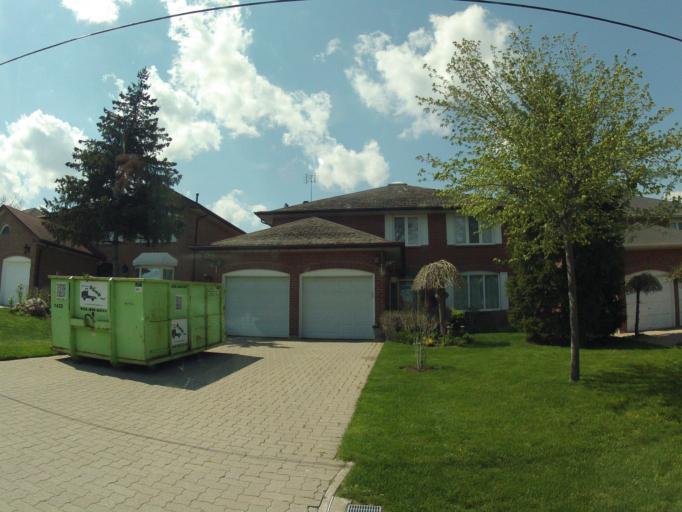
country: CA
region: Ontario
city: Mississauga
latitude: 43.5728
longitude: -79.6975
